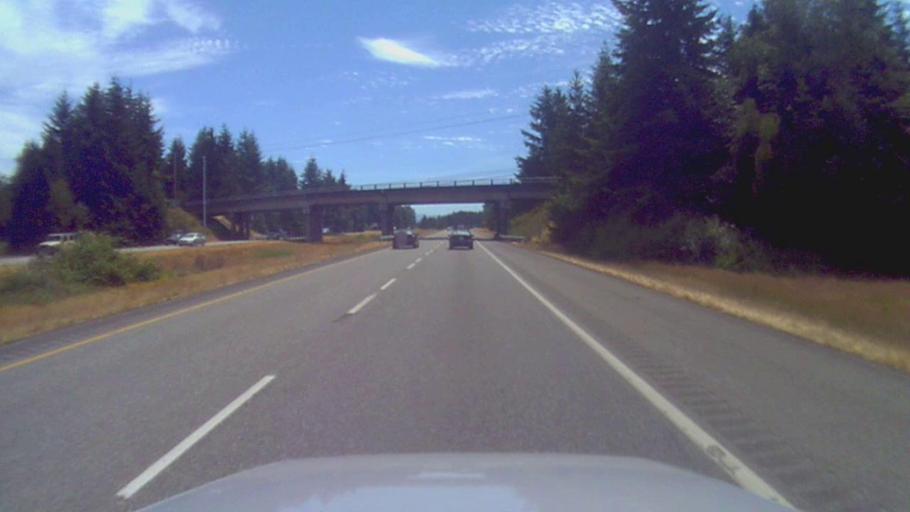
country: US
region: Washington
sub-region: Whatcom County
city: Ferndale
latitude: 48.8923
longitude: -122.5979
